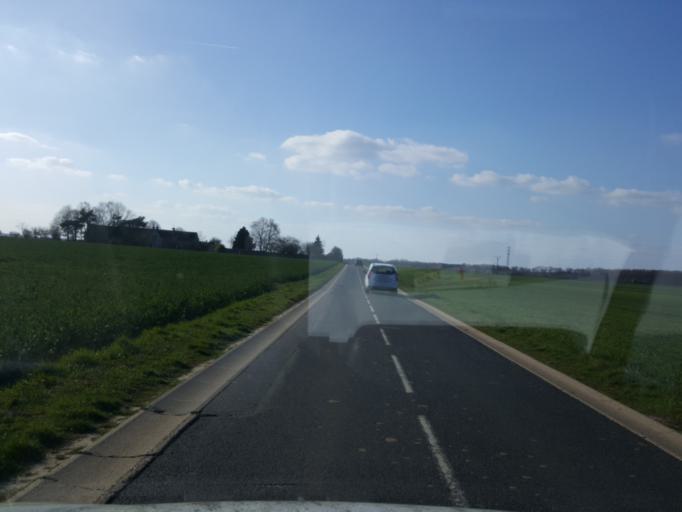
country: FR
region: Ile-de-France
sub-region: Departement des Yvelines
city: Rambouillet
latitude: 48.6222
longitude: 1.8085
